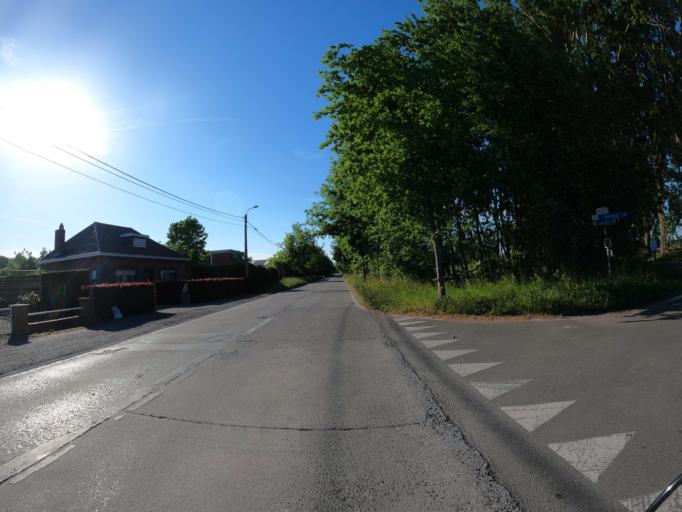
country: BE
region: Flanders
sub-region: Provincie Oost-Vlaanderen
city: Nazareth
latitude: 50.9687
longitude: 3.5788
